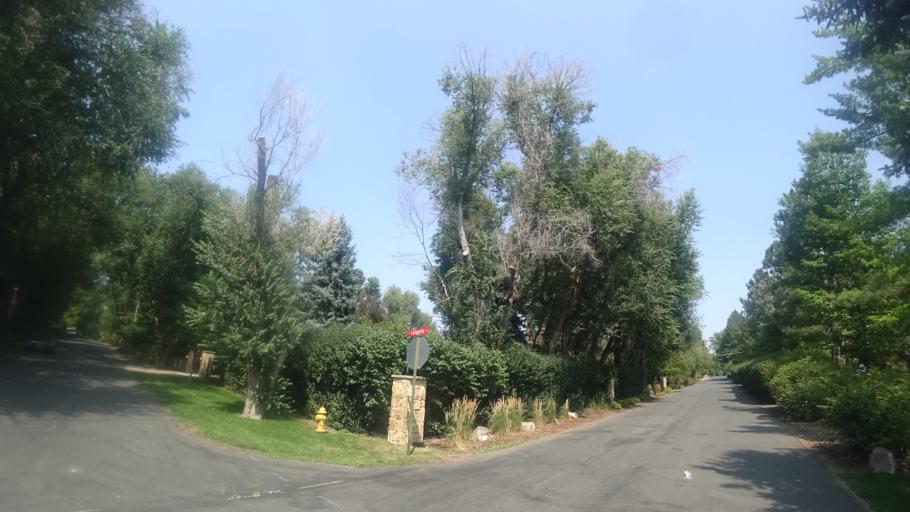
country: US
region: Colorado
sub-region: Arapahoe County
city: Cherry Hills Village
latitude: 39.6295
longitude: -104.9715
